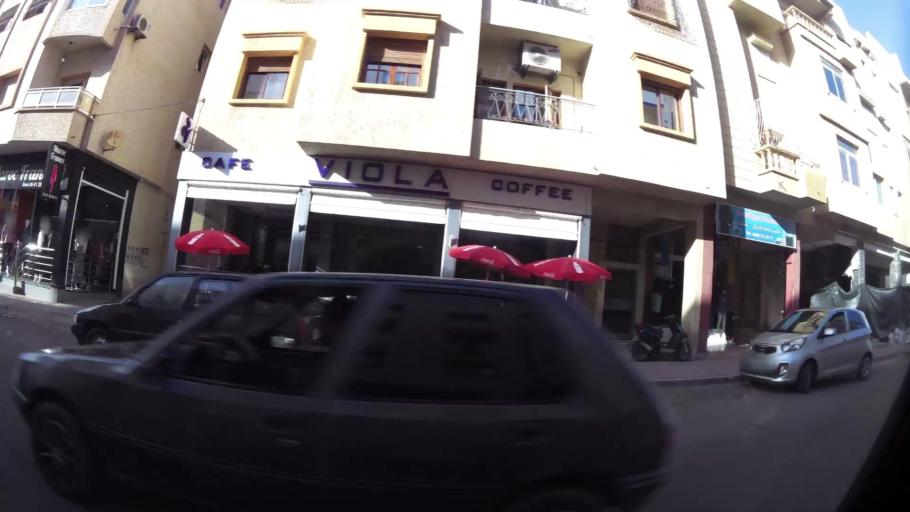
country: MA
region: Oued ed Dahab-Lagouira
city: Dakhla
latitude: 30.3987
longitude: -9.5475
